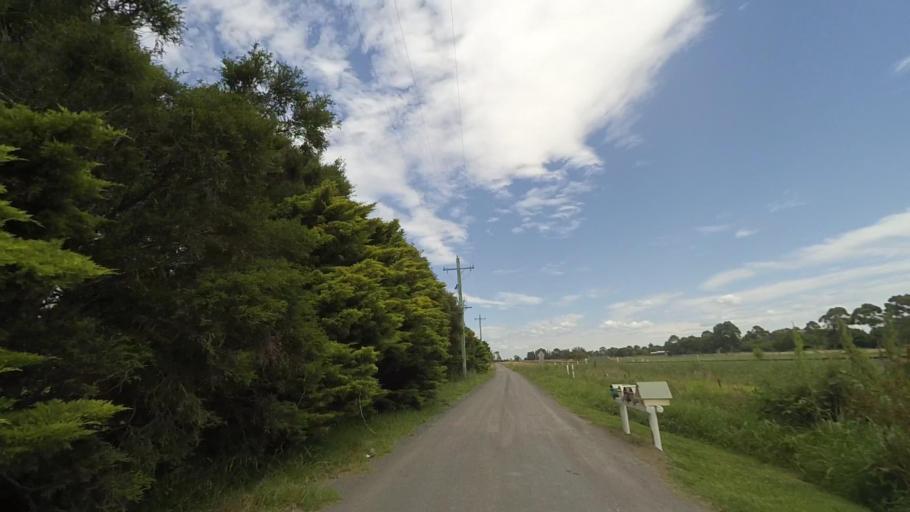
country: AU
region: New South Wales
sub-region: Shoalhaven Shire
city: Berry
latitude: -34.7903
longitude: 150.6797
